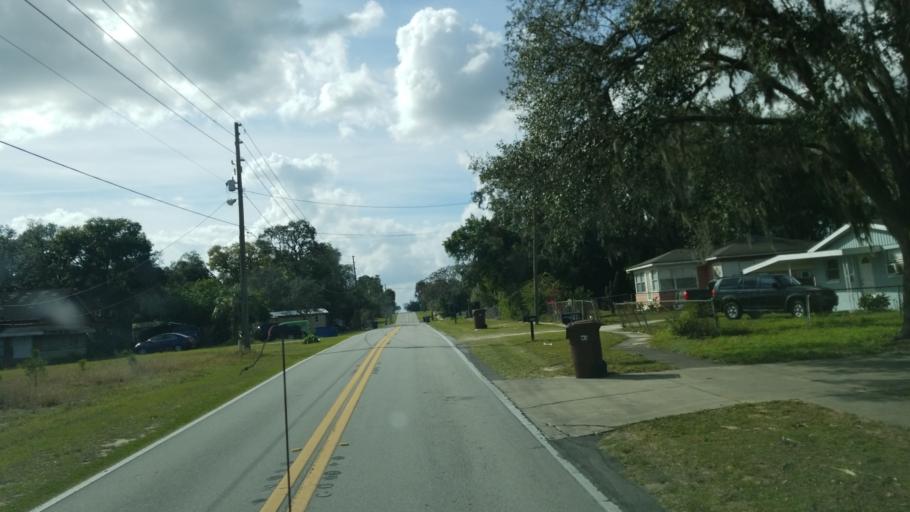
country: US
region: Florida
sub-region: Polk County
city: Davenport
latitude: 28.1540
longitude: -81.5949
